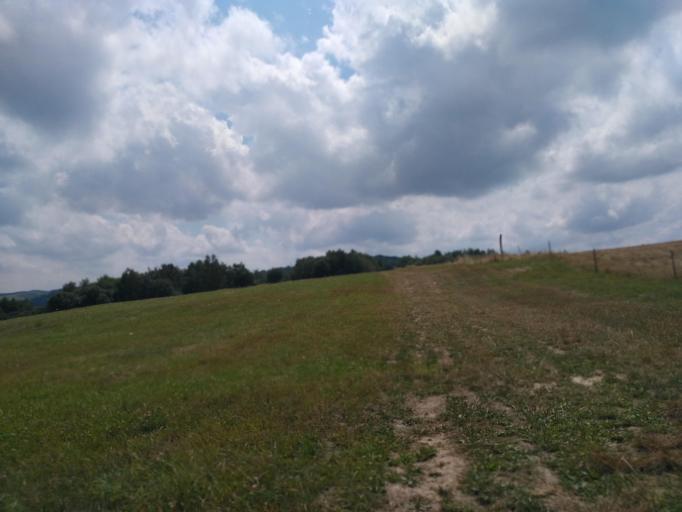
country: PL
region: Subcarpathian Voivodeship
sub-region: Powiat krosnienski
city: Iwonicz-Zdroj
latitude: 49.5773
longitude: 21.7778
